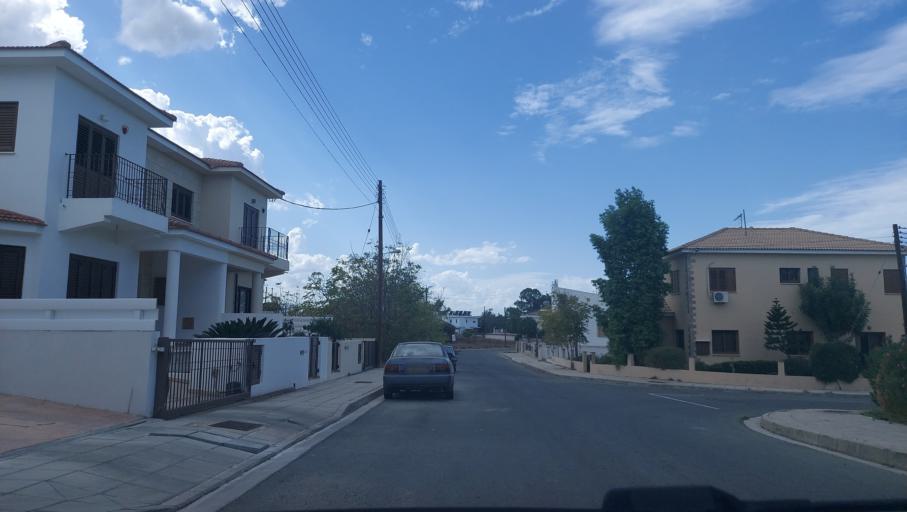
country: CY
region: Lefkosia
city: Pano Deftera
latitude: 35.0857
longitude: 33.2659
